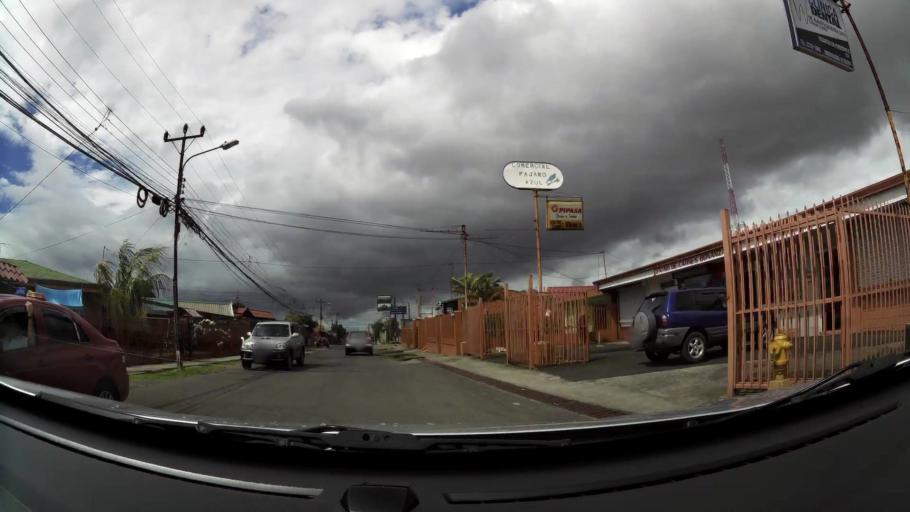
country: CR
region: Cartago
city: Concepcion
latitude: 9.9216
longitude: -83.9950
